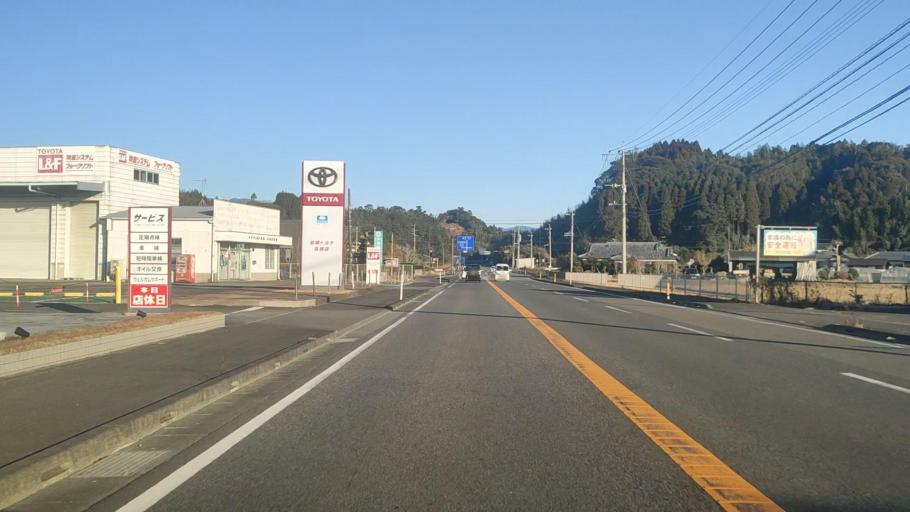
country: JP
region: Miyazaki
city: Takanabe
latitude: 32.1432
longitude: 131.5267
